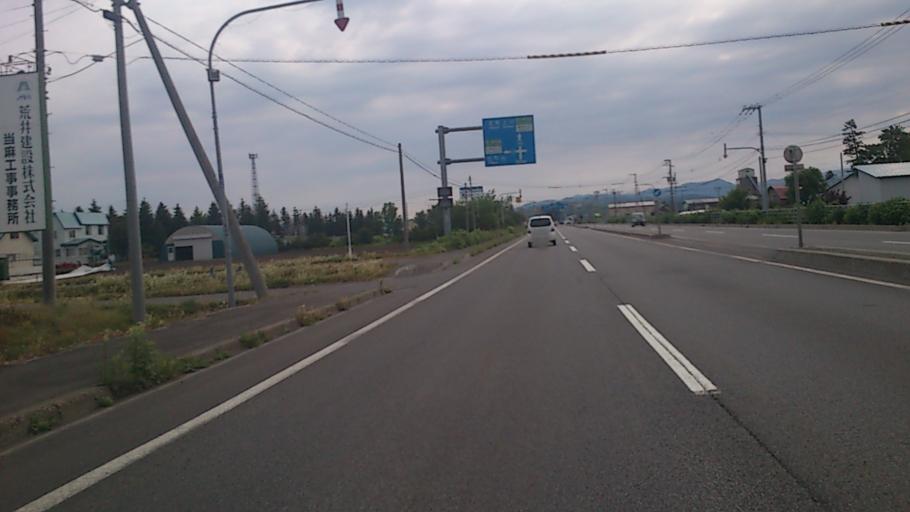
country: JP
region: Hokkaido
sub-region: Asahikawa-shi
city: Asahikawa
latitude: 43.8527
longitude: 142.5014
